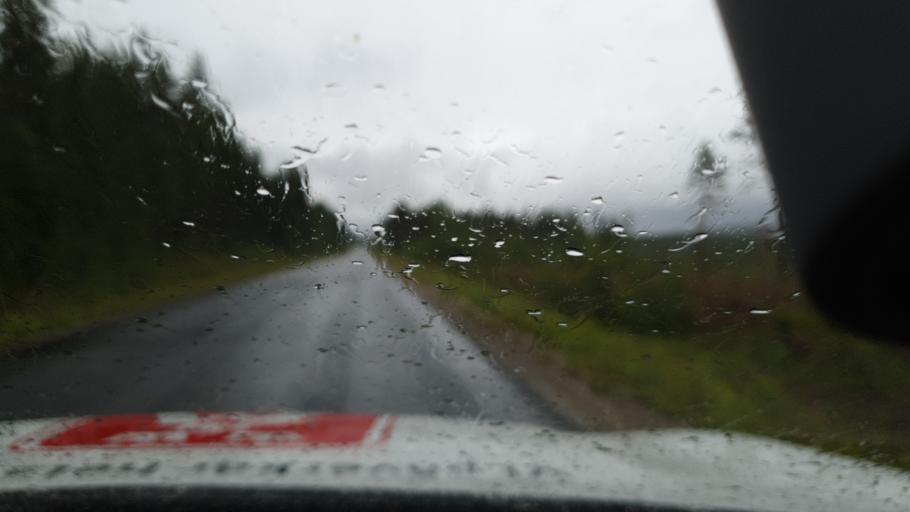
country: SE
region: Vaesterbotten
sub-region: Skelleftea Kommun
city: Langsele
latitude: 64.5646
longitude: 19.9300
